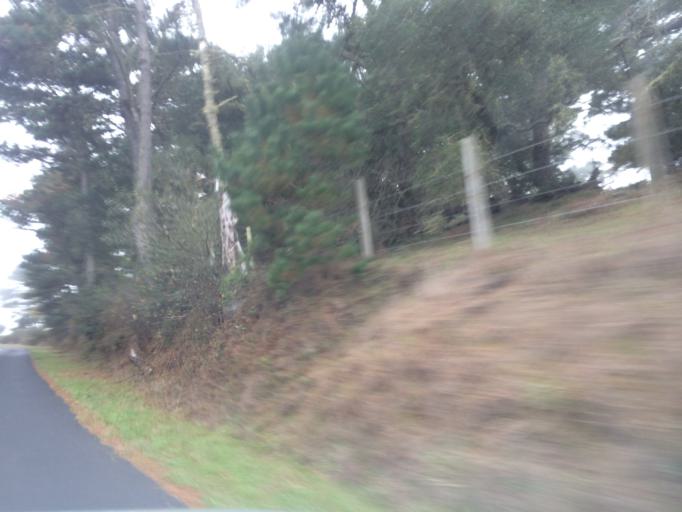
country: US
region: California
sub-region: Marin County
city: Inverness
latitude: 38.1190
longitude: -122.8967
